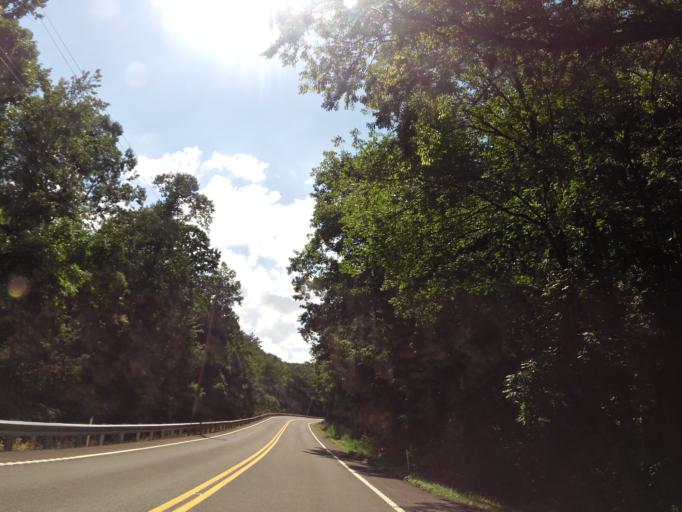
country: US
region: Tennessee
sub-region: Cumberland County
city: Fairfield Glade
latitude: 35.8846
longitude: -84.8258
